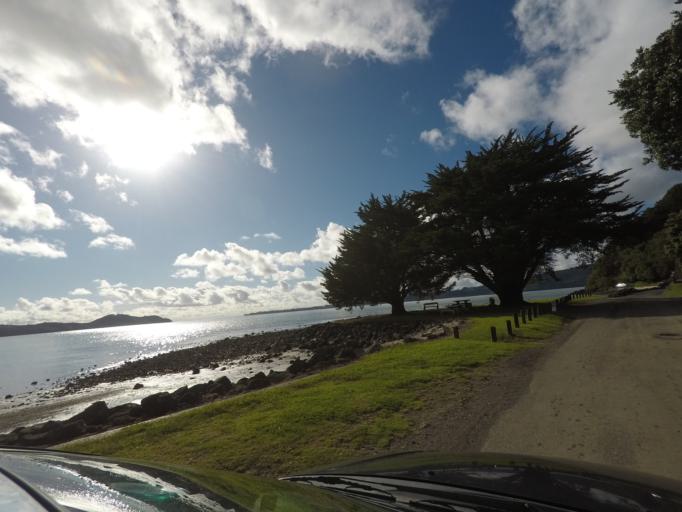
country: NZ
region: Auckland
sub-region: Auckland
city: Titirangi
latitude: -37.0161
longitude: 174.5583
